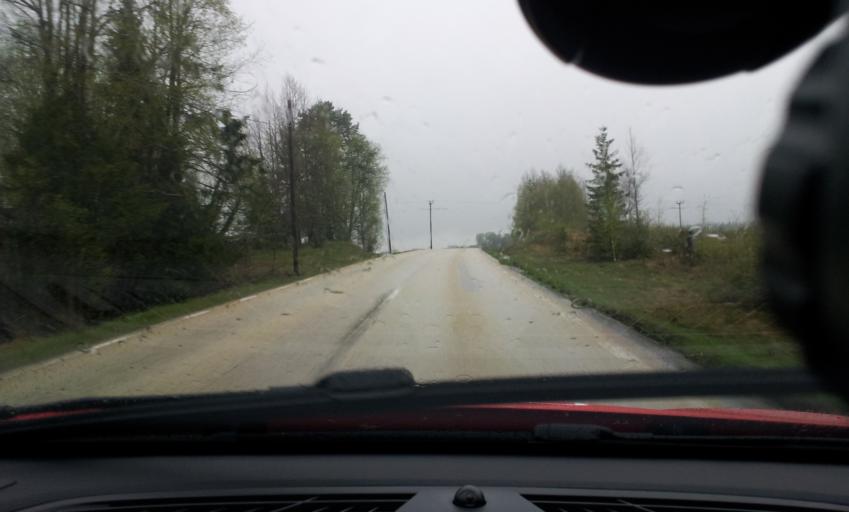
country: SE
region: Jaemtland
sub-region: Bergs Kommun
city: Hoverberg
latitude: 62.9860
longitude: 14.3404
